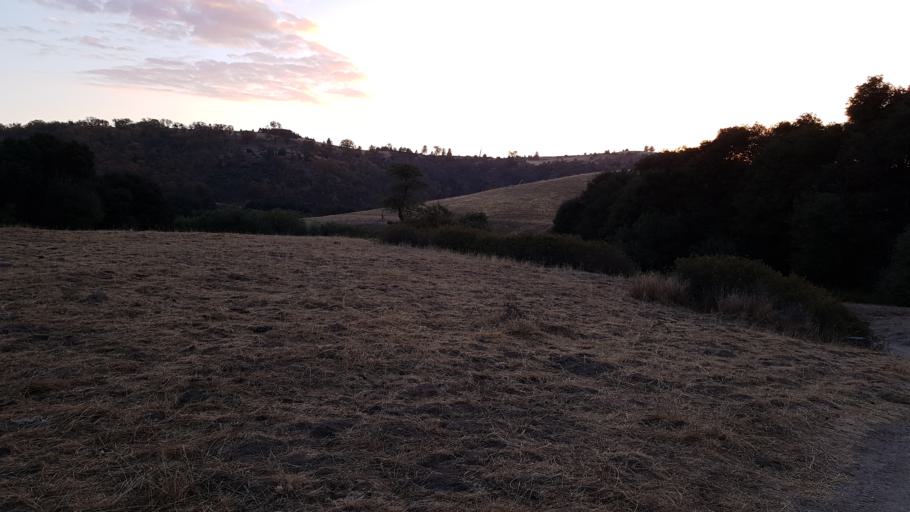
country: US
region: California
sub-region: San Diego County
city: Julian
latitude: 33.1199
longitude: -116.6040
